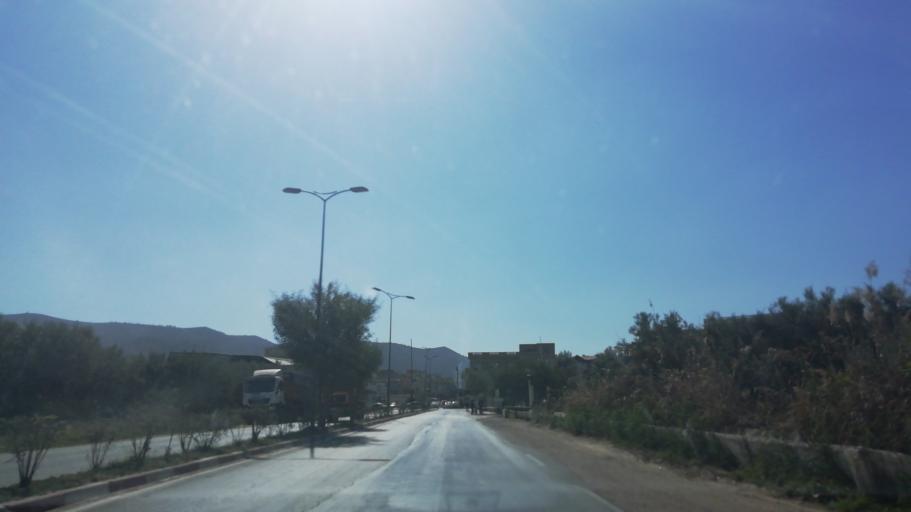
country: DZ
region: Mascara
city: Sig
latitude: 35.5312
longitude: -0.2025
